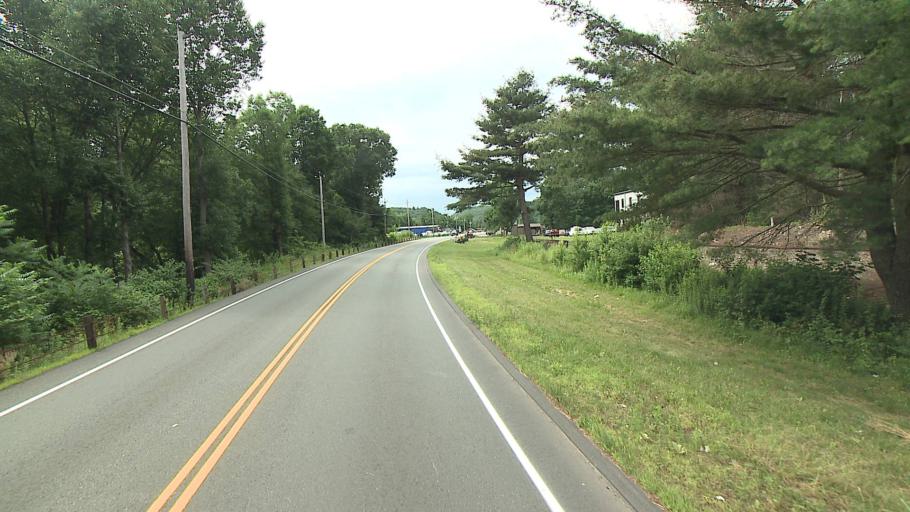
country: US
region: Connecticut
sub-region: Litchfield County
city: Torrington
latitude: 41.7688
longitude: -73.1172
